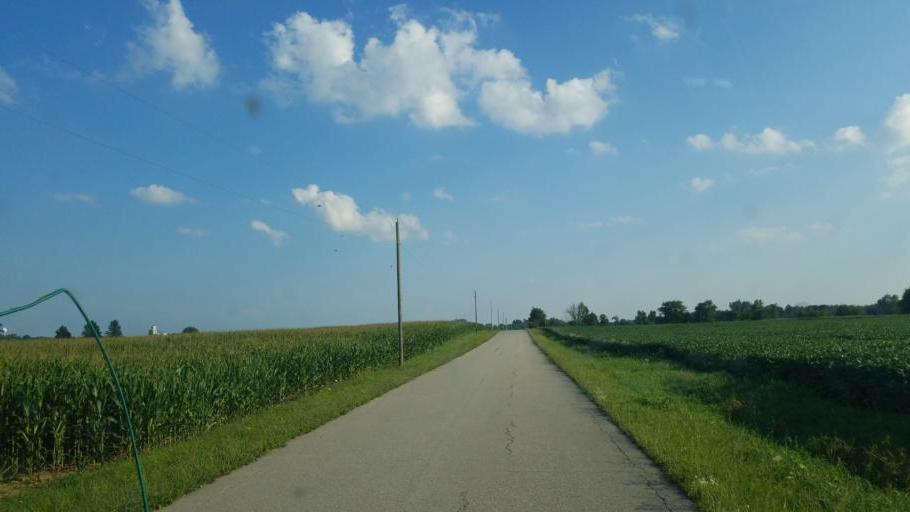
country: US
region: Ohio
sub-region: Crawford County
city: Galion
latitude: 40.8046
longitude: -82.8684
